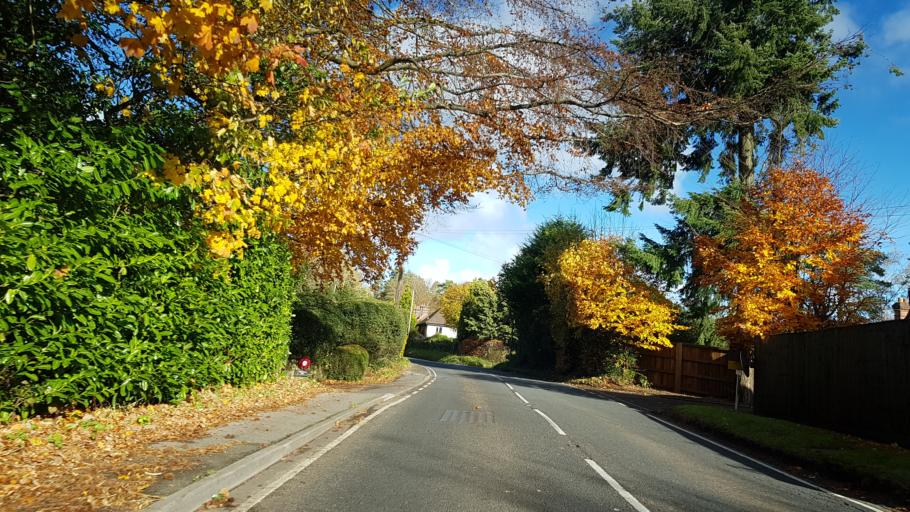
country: GB
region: England
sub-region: Surrey
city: Hindhead
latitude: 51.1056
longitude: -0.7341
